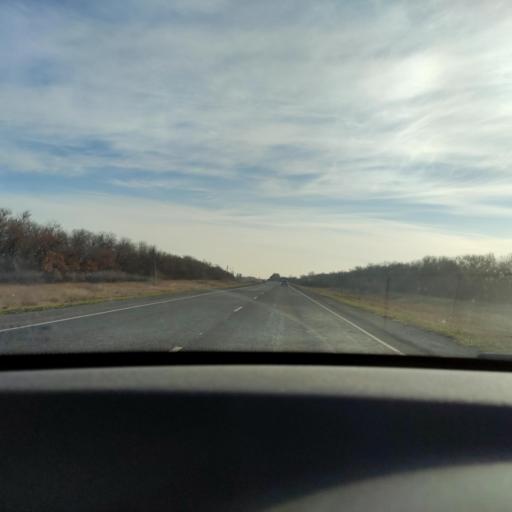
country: RU
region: Samara
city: Krasnoarmeyskoye
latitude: 52.7872
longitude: 50.0181
